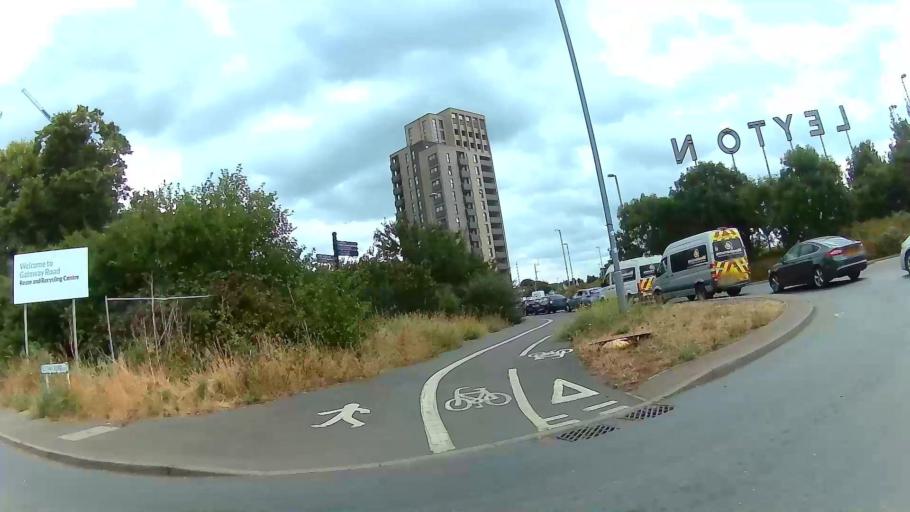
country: GB
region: England
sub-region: Greater London
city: Walthamstow
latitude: 51.5577
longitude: -0.0160
